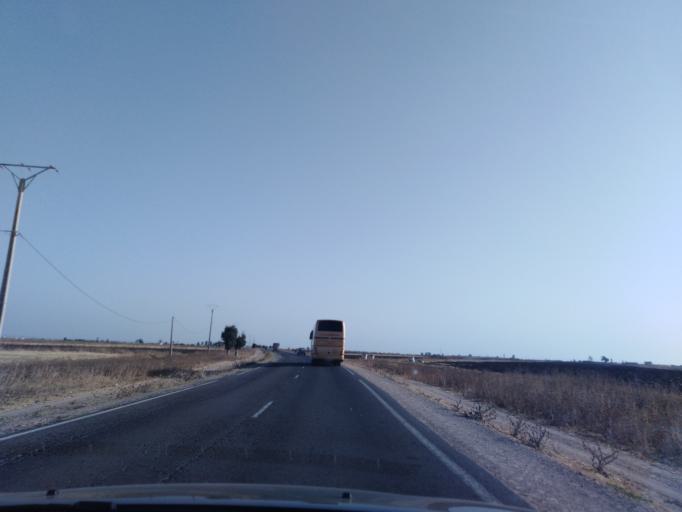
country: MA
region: Doukkala-Abda
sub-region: Safi
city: Youssoufia
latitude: 32.4853
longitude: -8.7674
